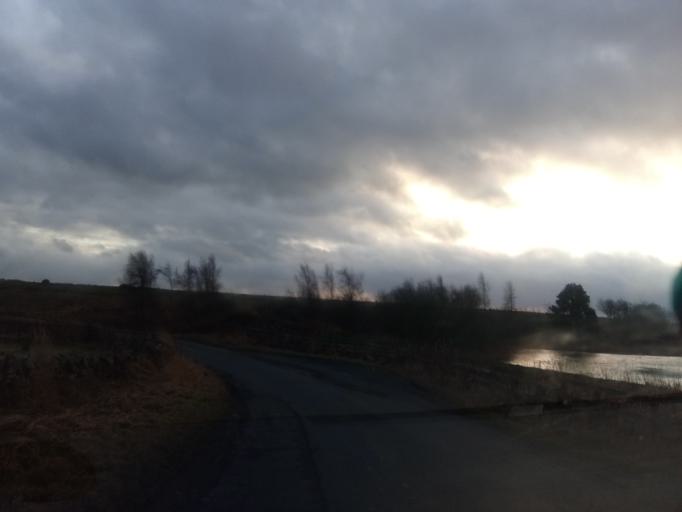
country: GB
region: Scotland
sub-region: The Scottish Borders
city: Selkirk
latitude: 55.5549
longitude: -2.7847
